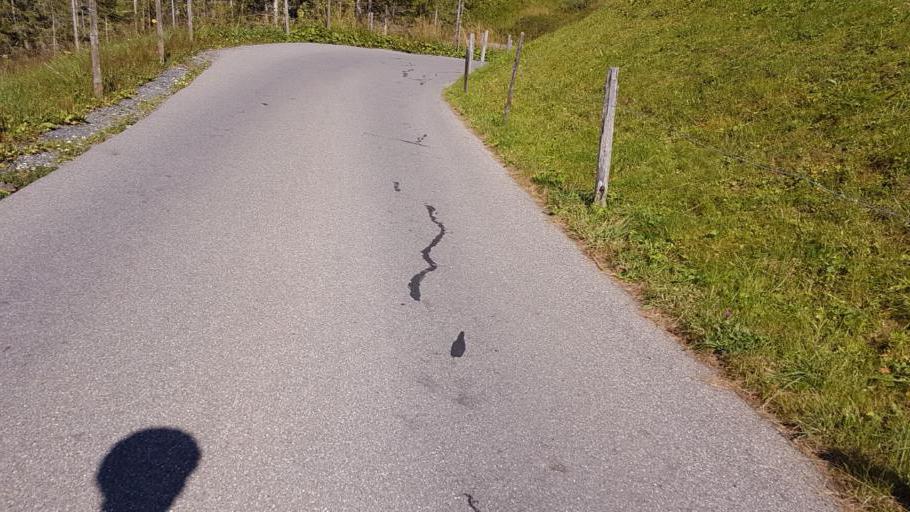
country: CH
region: Bern
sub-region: Frutigen-Niedersimmental District
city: Adelboden
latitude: 46.5209
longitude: 7.6070
